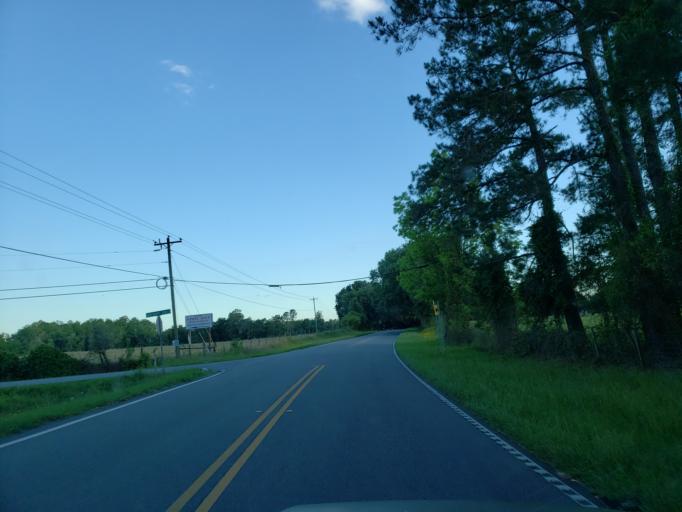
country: US
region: Georgia
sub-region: Lowndes County
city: Valdosta
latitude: 30.7175
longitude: -83.2430
